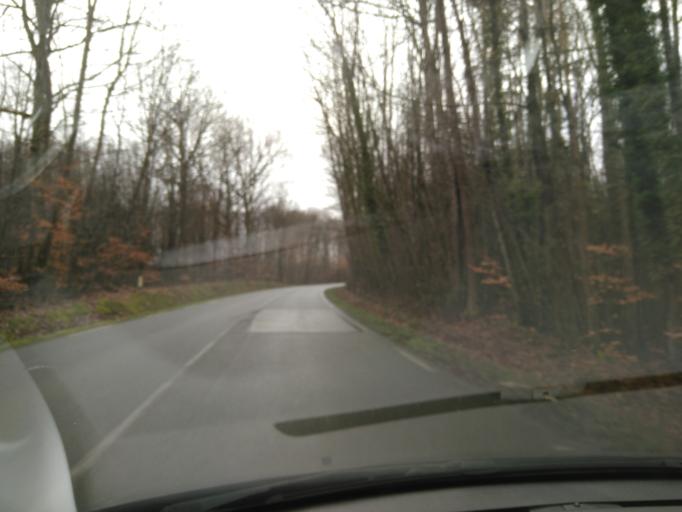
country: FR
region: Limousin
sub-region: Departement de la Haute-Vienne
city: Solignac
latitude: 45.7257
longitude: 1.2580
